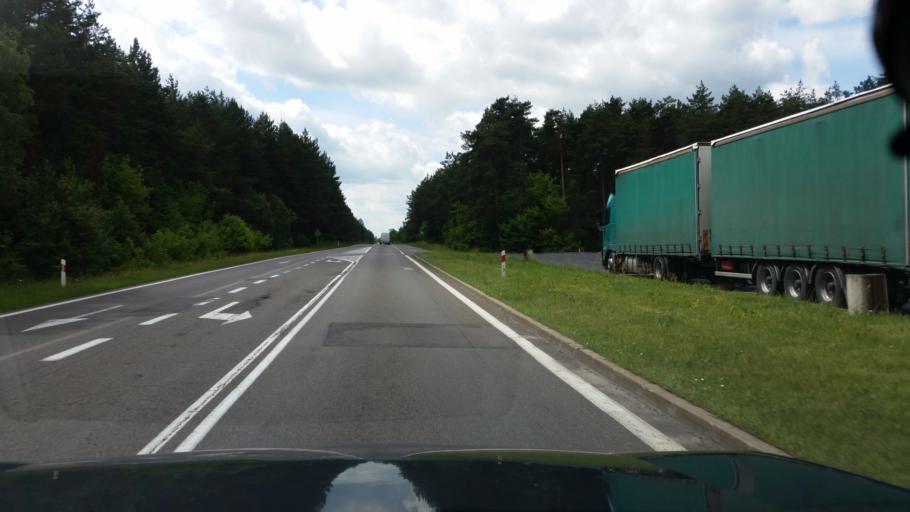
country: PL
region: Podlasie
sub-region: Powiat kolnenski
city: Stawiski
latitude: 53.4457
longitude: 22.1824
